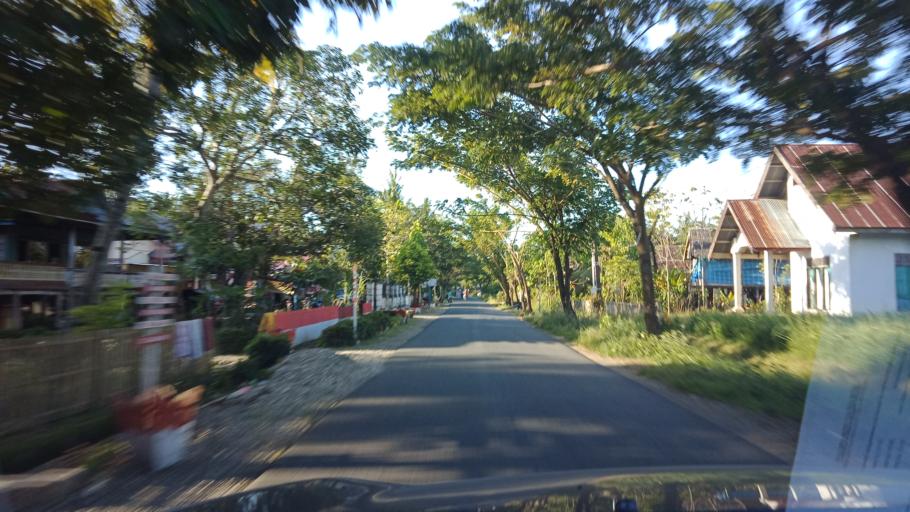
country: ID
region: South Sulawesi
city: Watampone
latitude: -4.4928
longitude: 120.3454
